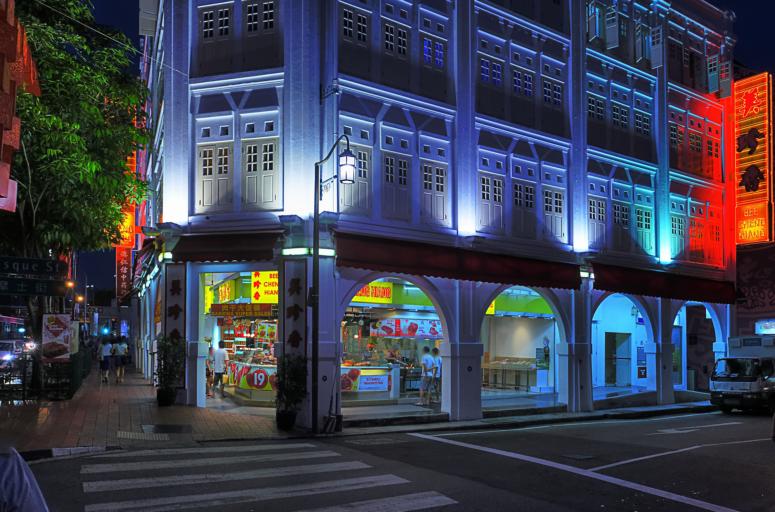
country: SG
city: Singapore
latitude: 1.2844
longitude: 103.8436
